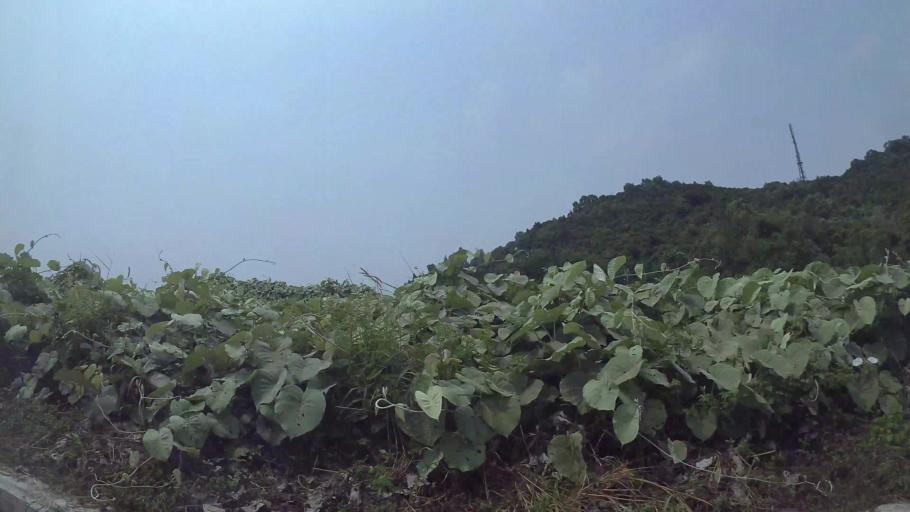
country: VN
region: Da Nang
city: Son Tra
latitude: 16.1003
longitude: 108.2758
